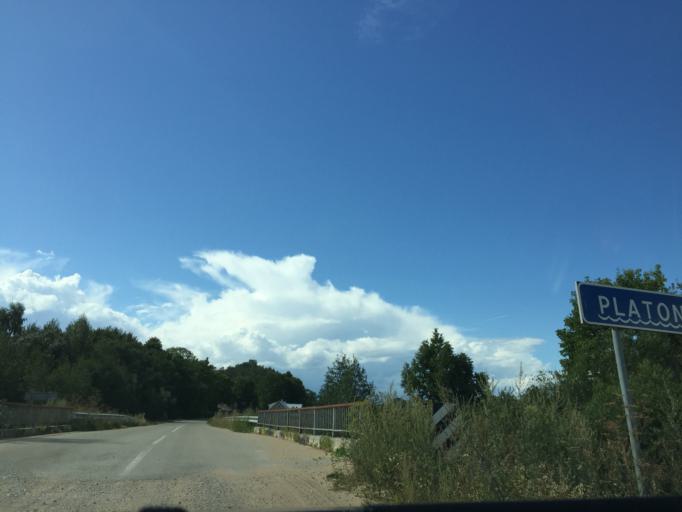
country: LT
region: Siauliu apskritis
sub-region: Joniskis
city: Joniskis
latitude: 56.3281
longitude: 23.5774
